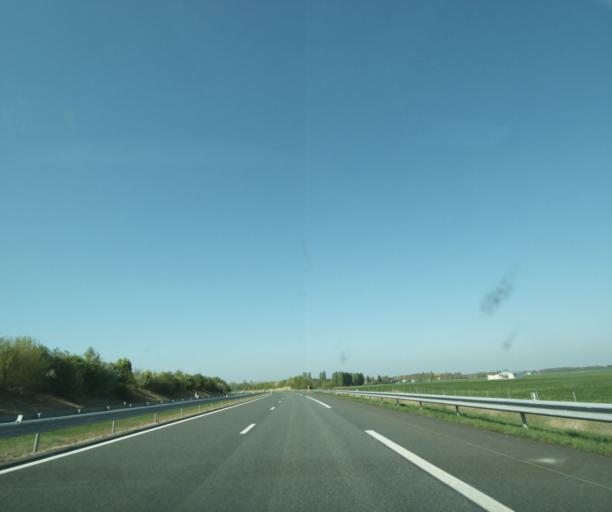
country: FR
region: Centre
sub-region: Departement du Loiret
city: Vimory
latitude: 47.9576
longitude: 2.6747
